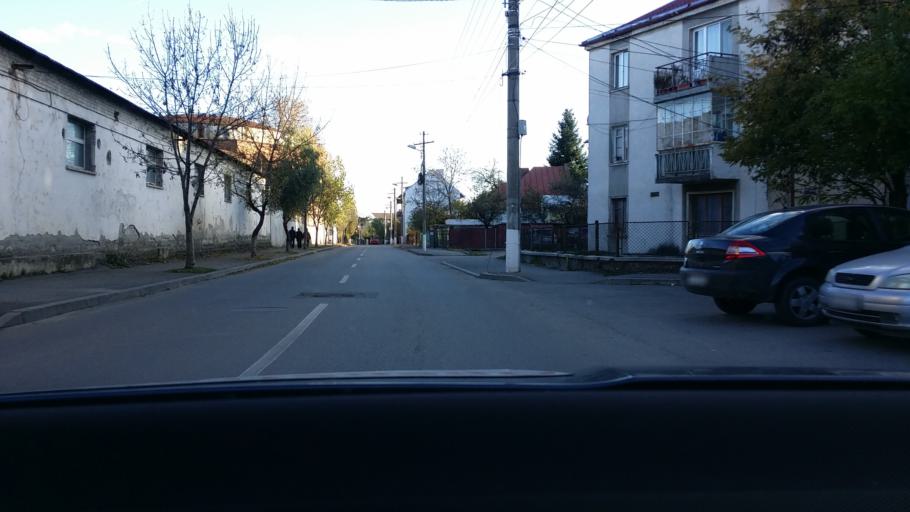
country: RO
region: Prahova
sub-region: Municipiul Campina
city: Campina
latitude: 45.1315
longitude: 25.7347
